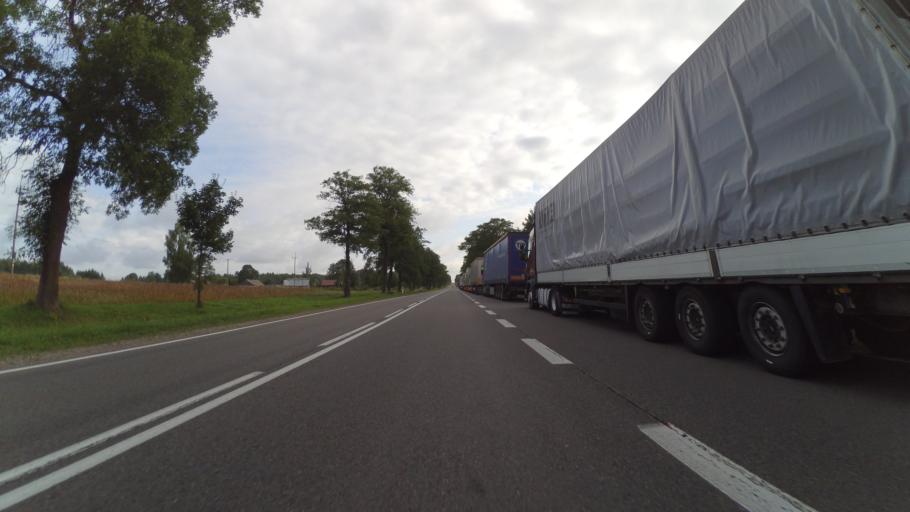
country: PL
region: Podlasie
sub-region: Powiat sokolski
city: Kuznica
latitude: 53.4781
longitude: 23.6010
